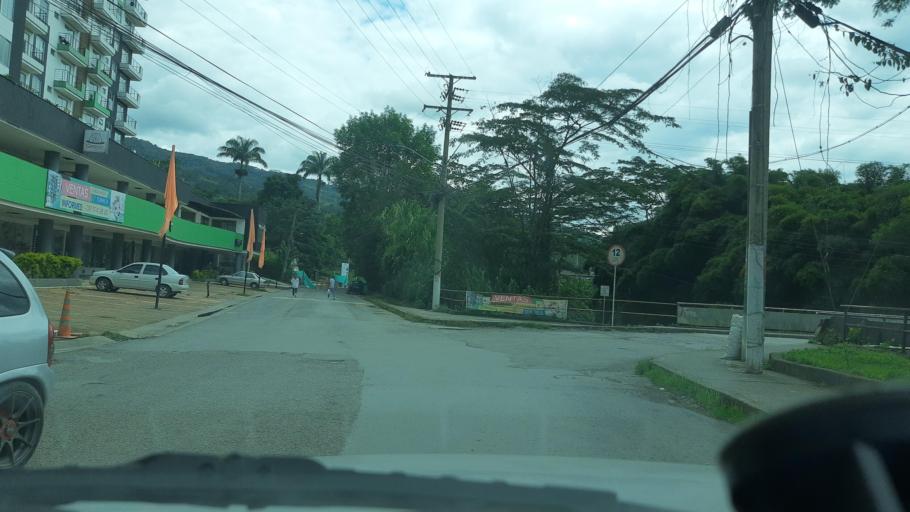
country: CO
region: Boyaca
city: Moniquira
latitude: 5.8781
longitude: -73.5747
